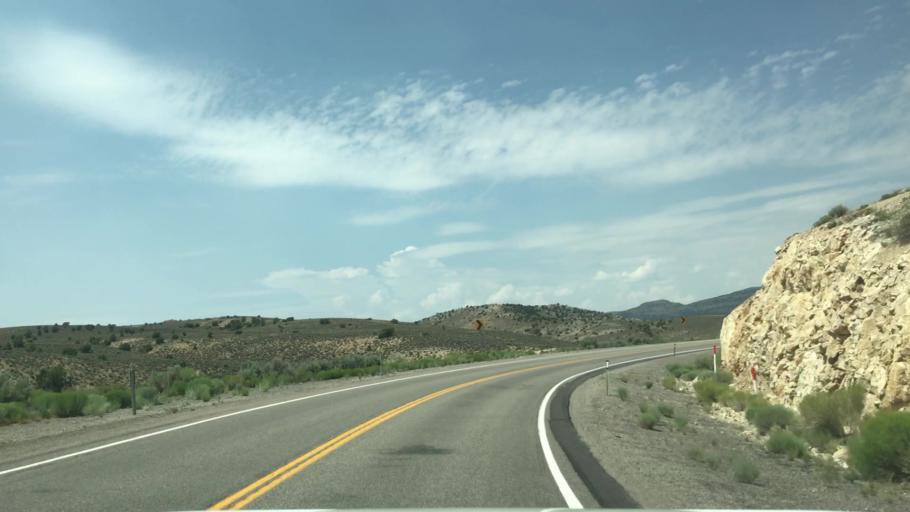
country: US
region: Nevada
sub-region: White Pine County
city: Ely
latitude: 39.3516
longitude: -115.3636
